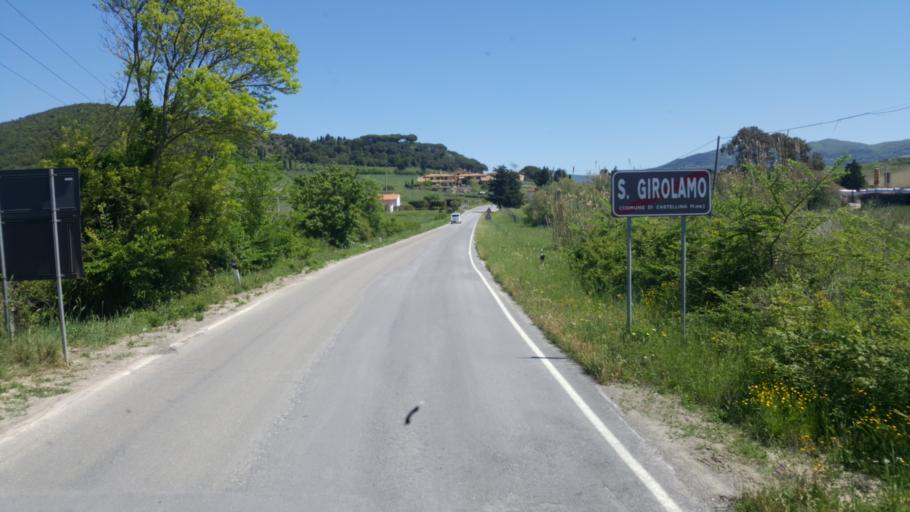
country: IT
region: Tuscany
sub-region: Provincia di Livorno
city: Rosignano Marittimo
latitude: 43.4106
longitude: 10.5003
